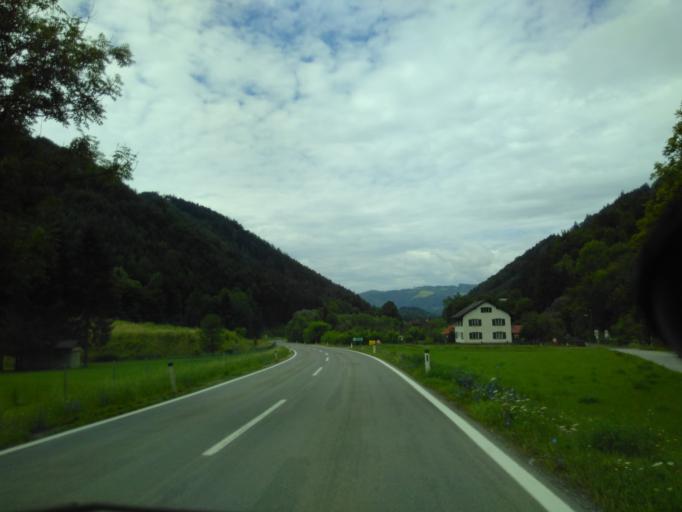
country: AT
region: Styria
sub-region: Politischer Bezirk Graz-Umgebung
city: Schrems bei Frohnleiten
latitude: 47.2771
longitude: 15.3514
